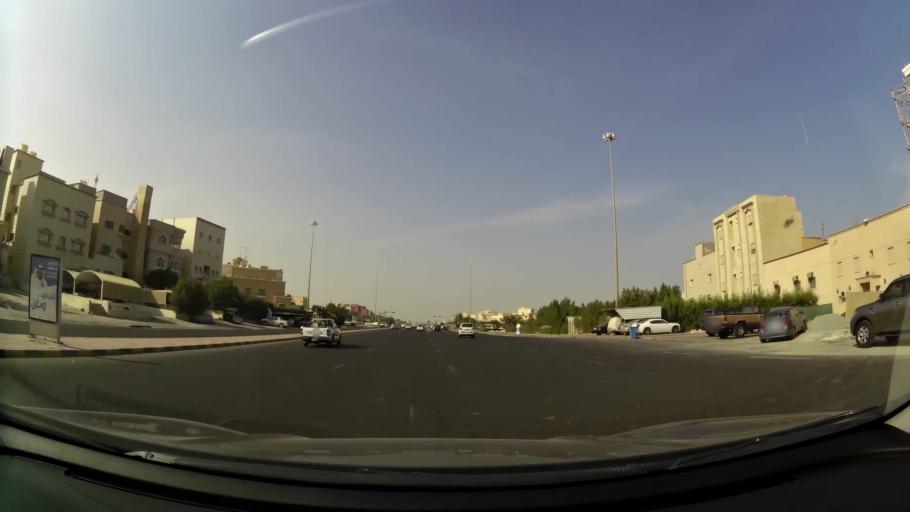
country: KW
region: Mubarak al Kabir
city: Mubarak al Kabir
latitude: 29.1783
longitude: 48.0836
